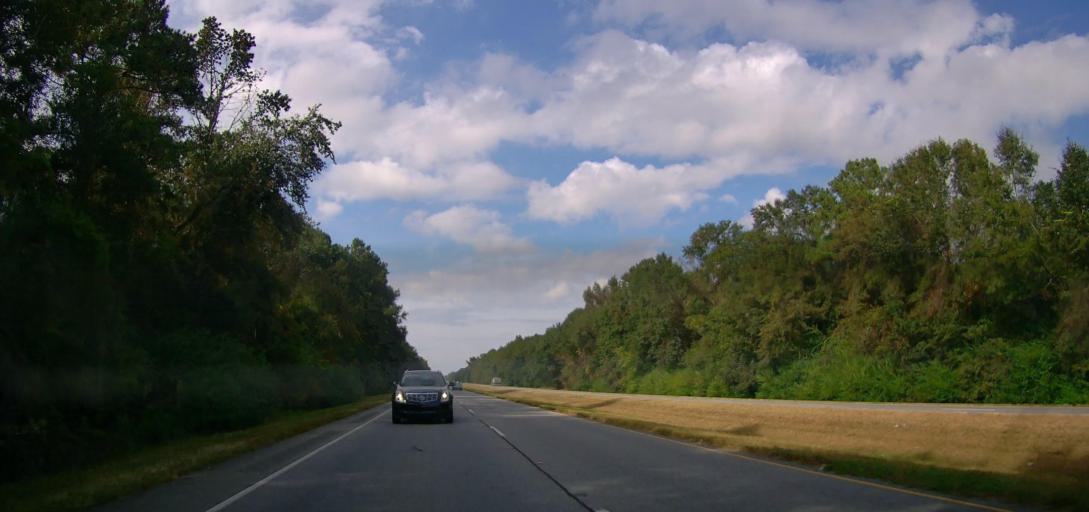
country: US
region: Georgia
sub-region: Mitchell County
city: Pelham
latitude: 31.1776
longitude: -84.1507
